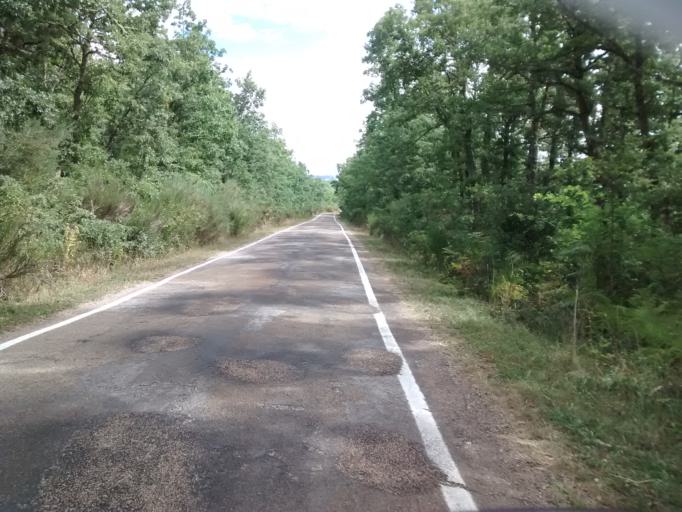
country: ES
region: Castille and Leon
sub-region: Provincia de Palencia
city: Polentinos
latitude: 42.9353
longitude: -4.4642
